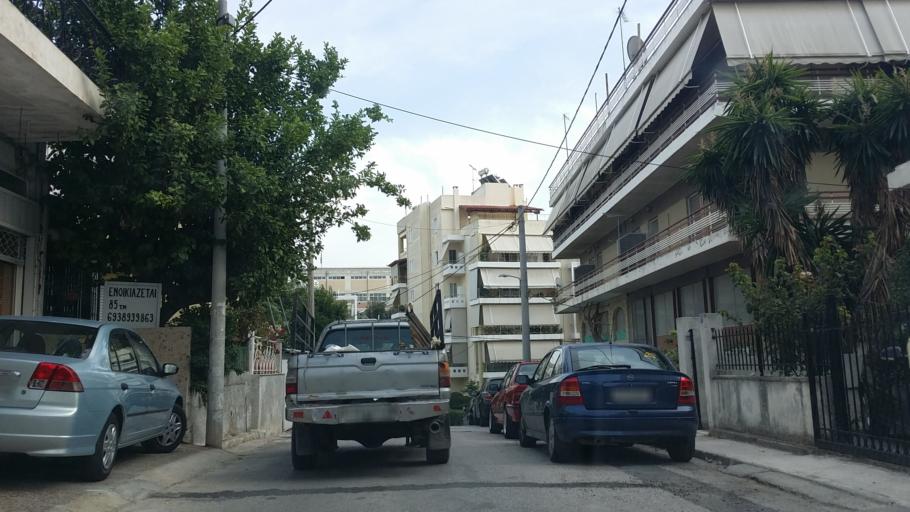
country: GR
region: Attica
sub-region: Nomarchia Athinas
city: Irakleio
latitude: 38.0547
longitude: 23.7583
